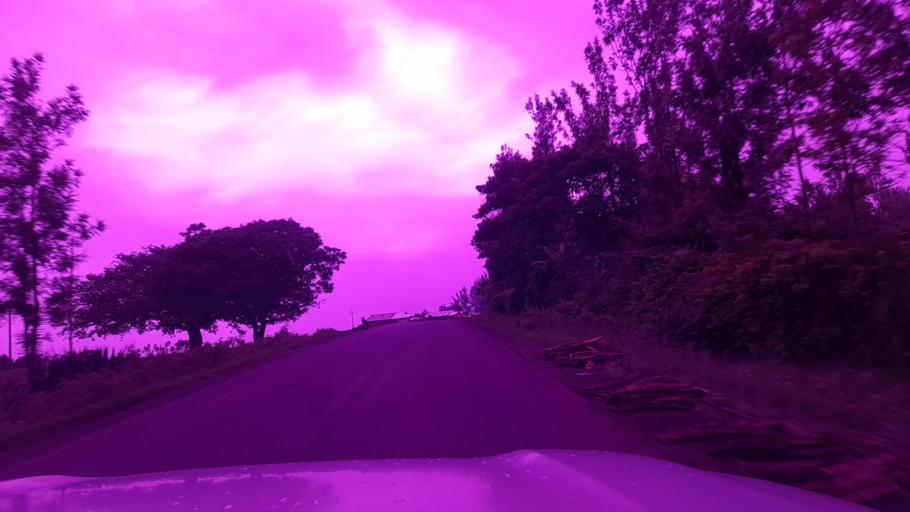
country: ET
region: Oromiya
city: Waliso
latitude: 8.1749
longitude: 37.5620
